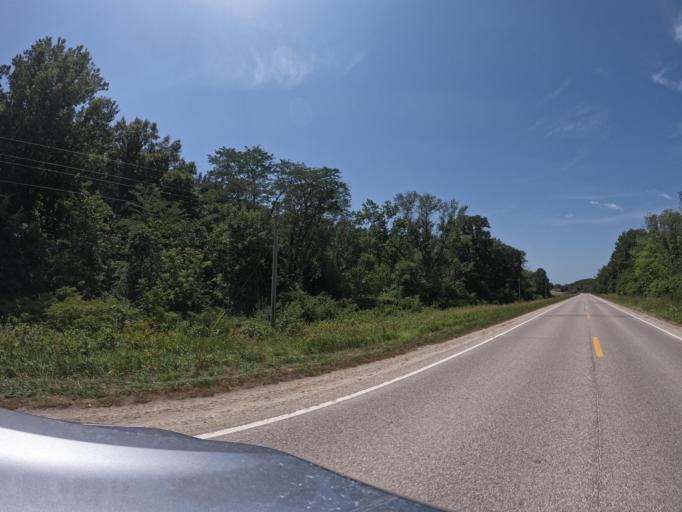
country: US
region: Iowa
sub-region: Henry County
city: Mount Pleasant
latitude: 40.9381
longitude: -91.5879
